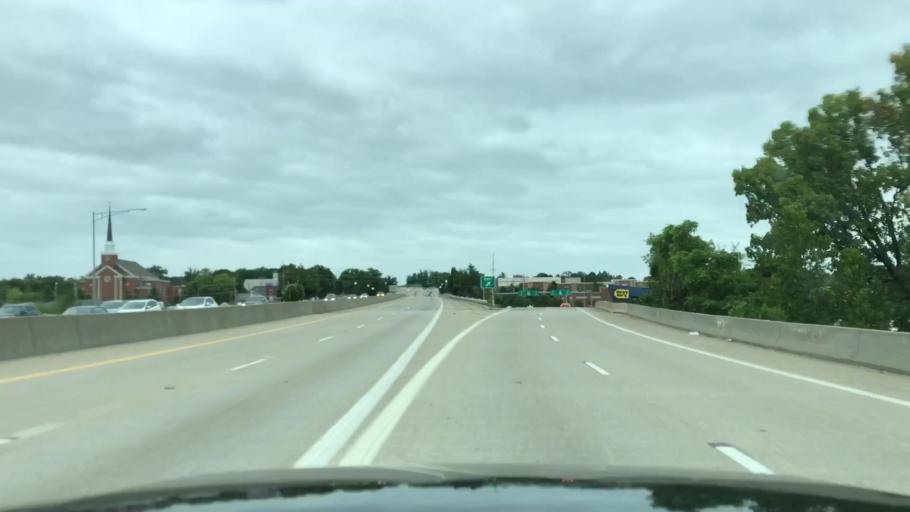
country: US
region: Missouri
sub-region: Saint Louis County
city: Manchester
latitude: 38.5902
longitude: -90.5086
